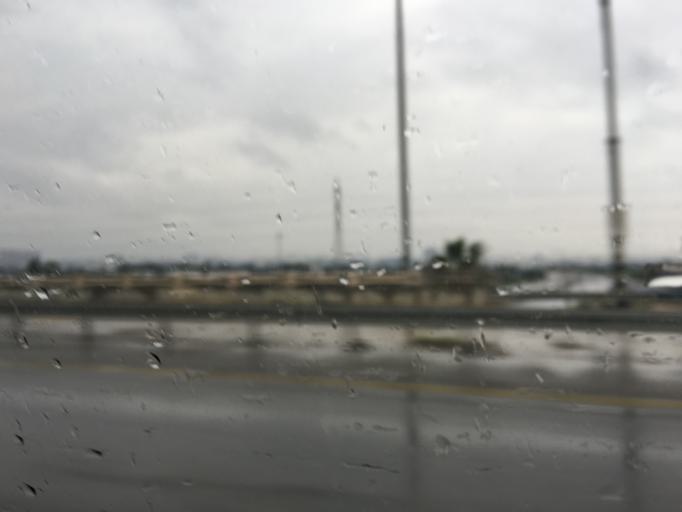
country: IL
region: Tel Aviv
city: Ramat HaSharon
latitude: 32.1249
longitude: 34.8549
